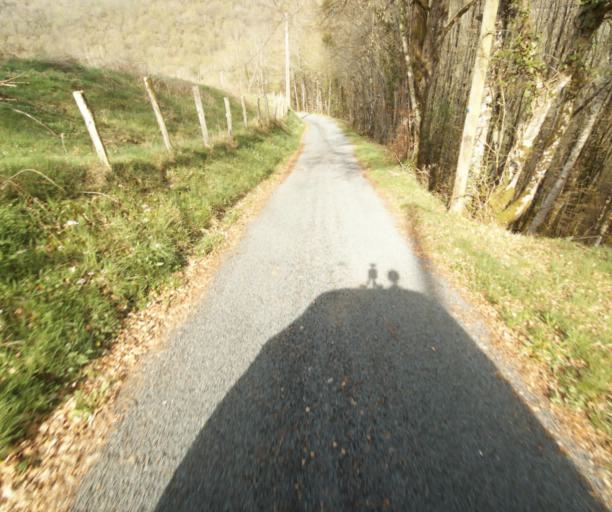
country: FR
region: Limousin
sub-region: Departement de la Correze
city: Naves
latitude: 45.3297
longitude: 1.8151
